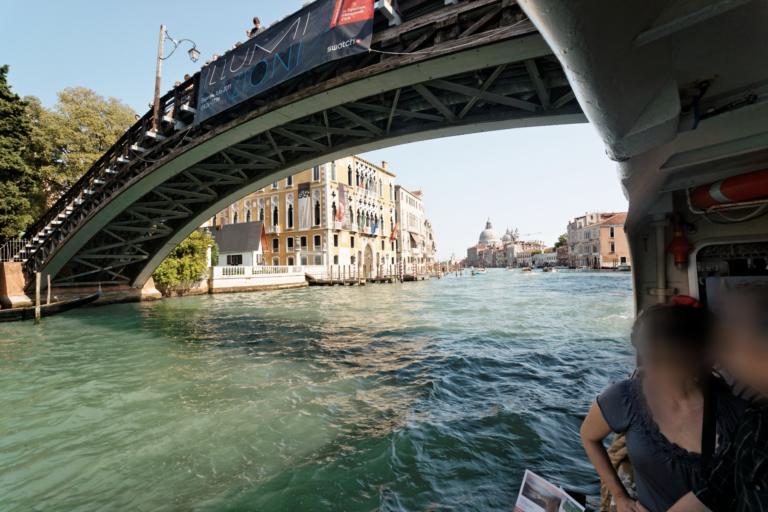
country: IT
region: Veneto
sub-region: Provincia di Venezia
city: Venice
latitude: 45.4317
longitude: 12.3288
